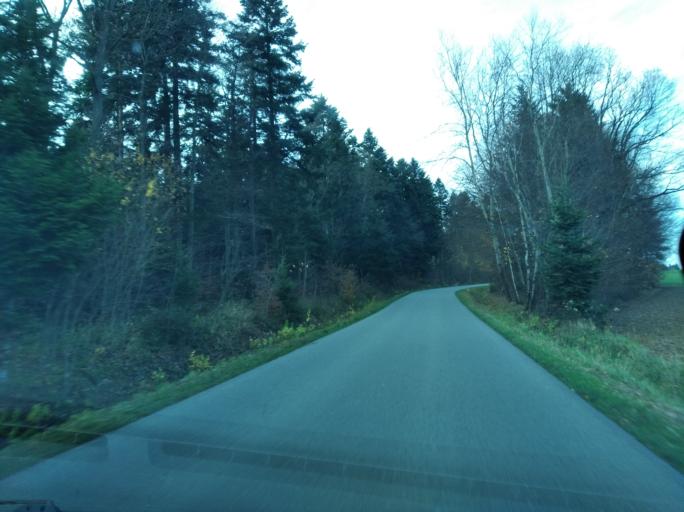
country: PL
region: Subcarpathian Voivodeship
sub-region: Powiat ropczycko-sedziszowski
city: Zagorzyce
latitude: 49.9542
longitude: 21.6957
